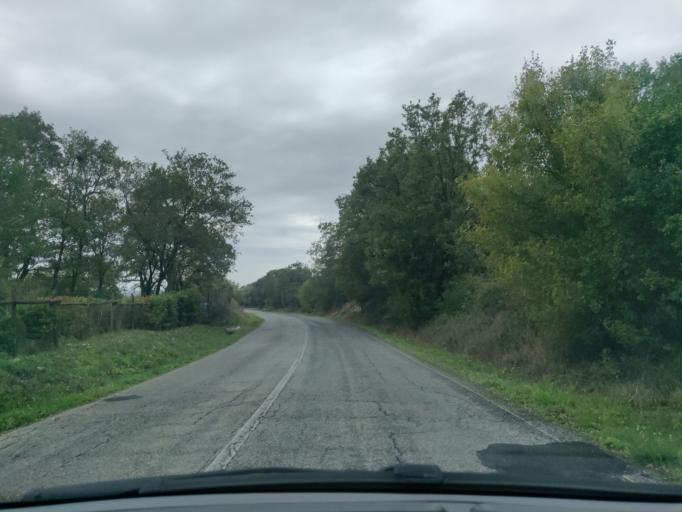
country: IT
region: Latium
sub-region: Citta metropolitana di Roma Capitale
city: Allumiere
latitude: 42.1346
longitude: 11.8698
